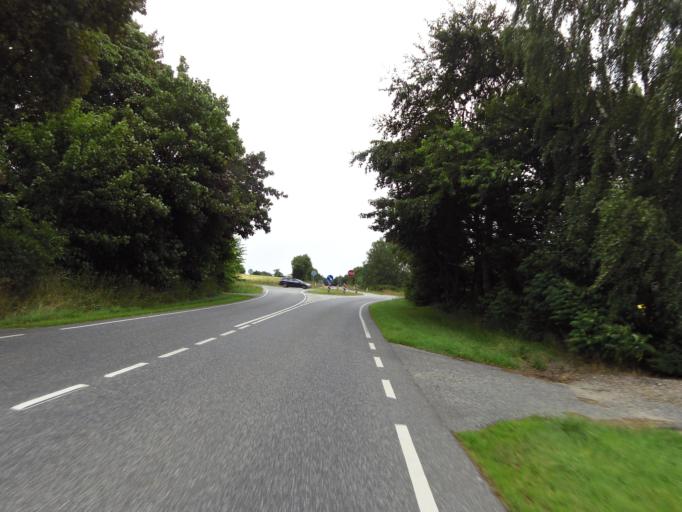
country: DK
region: South Denmark
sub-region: Tonder Kommune
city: Toftlund
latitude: 55.1680
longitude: 8.9646
